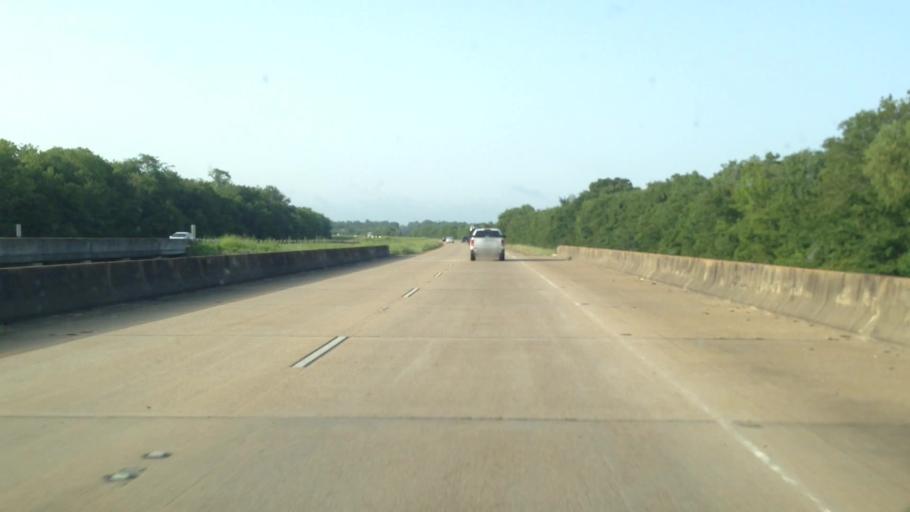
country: US
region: Louisiana
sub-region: Rapides Parish
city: Woodworth
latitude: 31.1985
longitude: -92.4744
